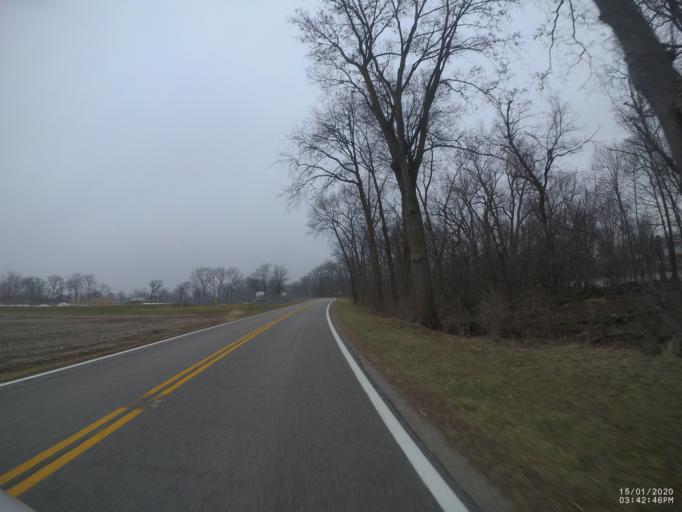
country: US
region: Ohio
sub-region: Sandusky County
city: Woodville
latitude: 41.4511
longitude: -83.3512
